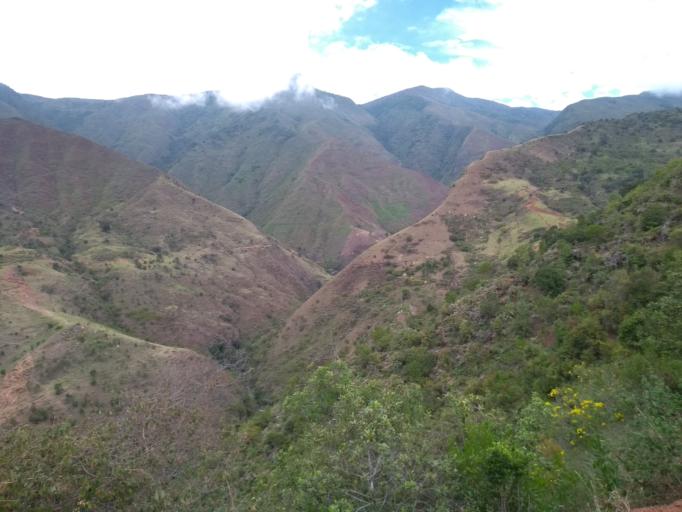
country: CO
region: Cesar
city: Manaure Balcon del Cesar
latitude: 10.1714
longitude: -73.0228
